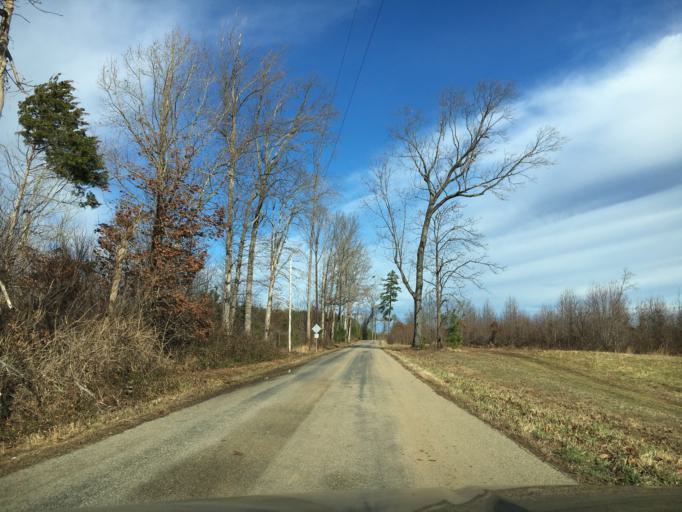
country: US
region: Virginia
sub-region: Nottoway County
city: Crewe
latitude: 37.2702
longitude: -78.2177
